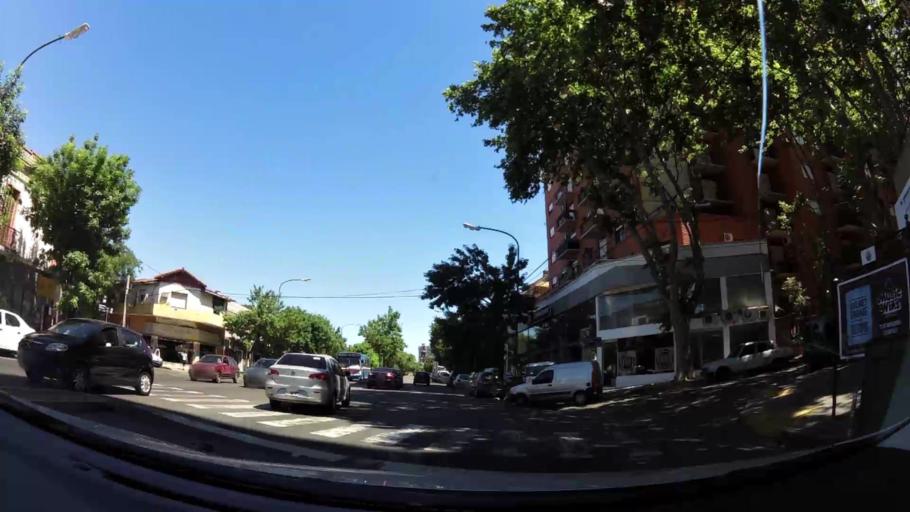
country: AR
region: Buenos Aires
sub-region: Partido de San Isidro
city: San Isidro
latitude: -34.4668
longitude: -58.5198
